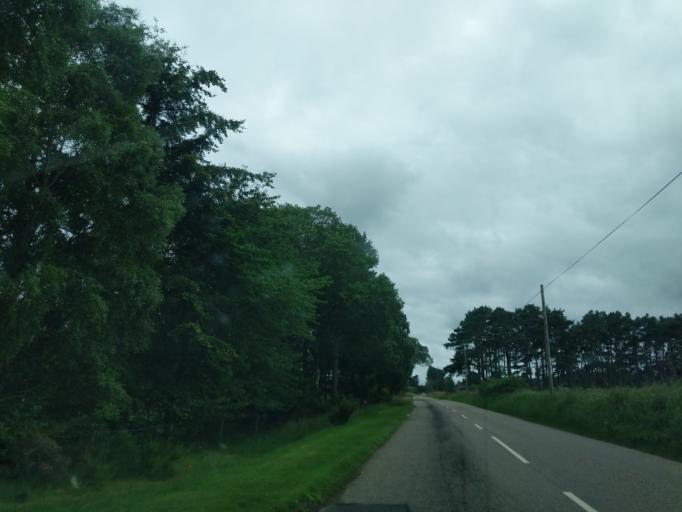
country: GB
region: Scotland
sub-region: Moray
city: Rothes
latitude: 57.4886
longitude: -3.2437
